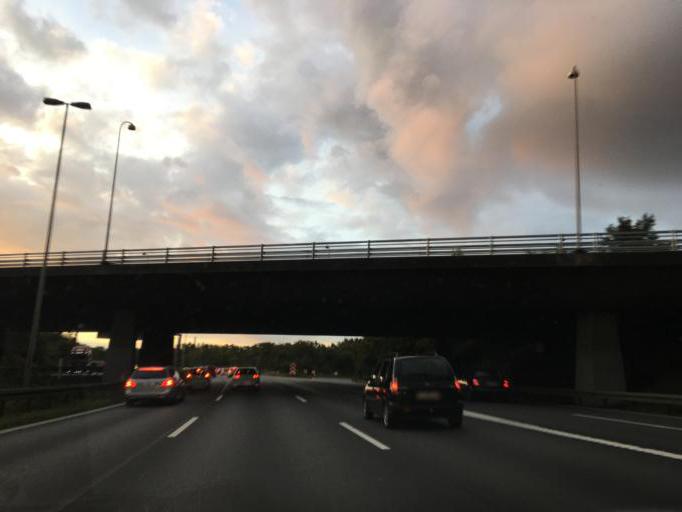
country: DK
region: Capital Region
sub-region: Brondby Kommune
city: Brondbyvester
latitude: 55.6182
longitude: 12.4454
